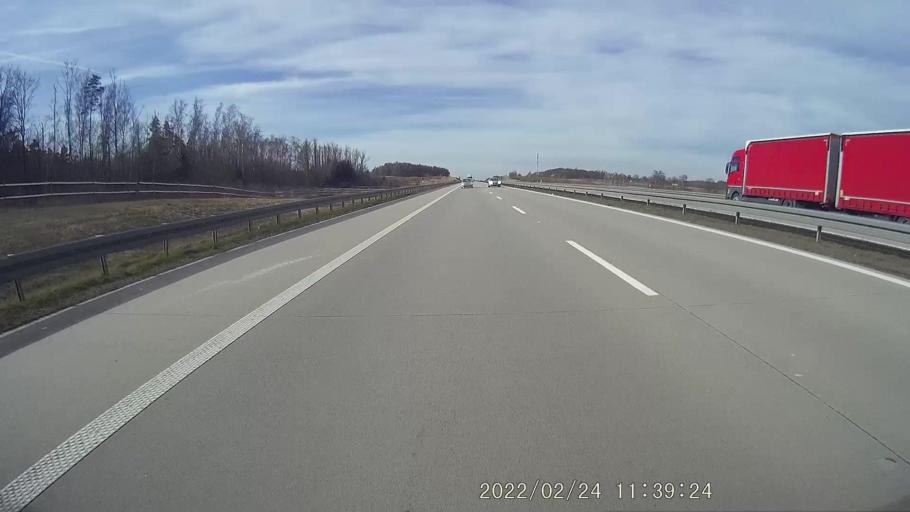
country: PL
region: Lower Silesian Voivodeship
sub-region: Powiat polkowicki
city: Przemkow
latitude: 51.5324
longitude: 15.8640
